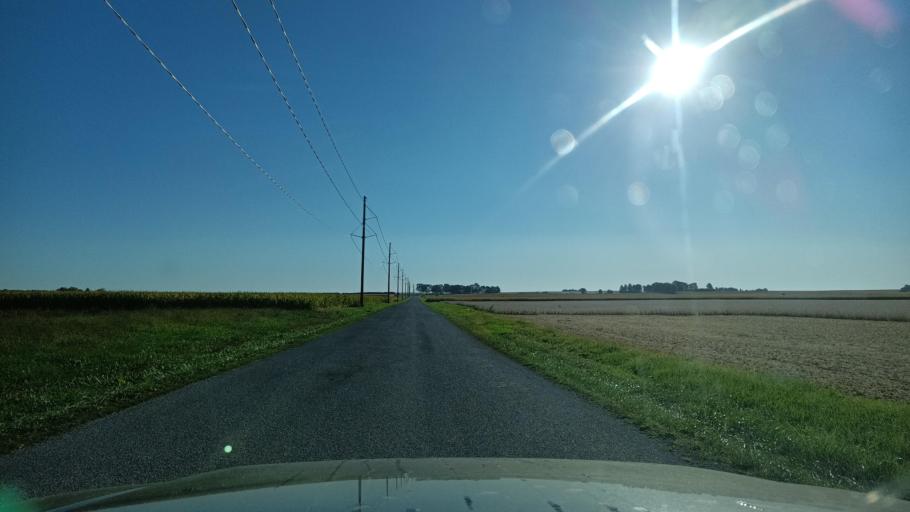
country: US
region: Illinois
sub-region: Champaign County
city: Savoy
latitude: 40.0546
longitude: -88.2054
